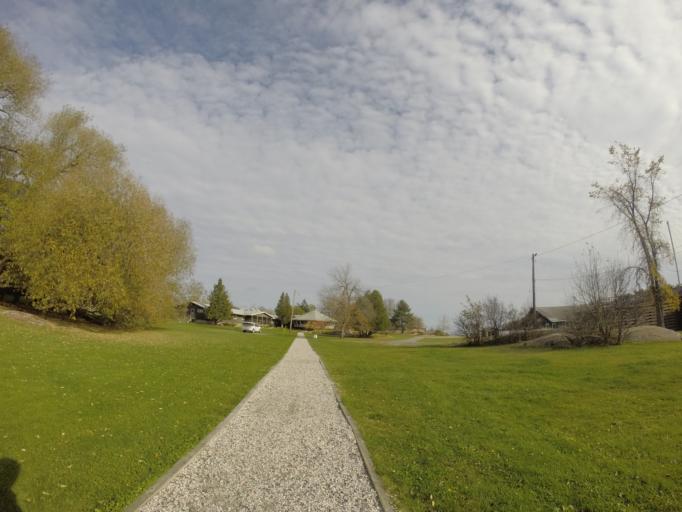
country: CA
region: Ontario
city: Espanola
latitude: 45.9694
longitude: -81.5083
